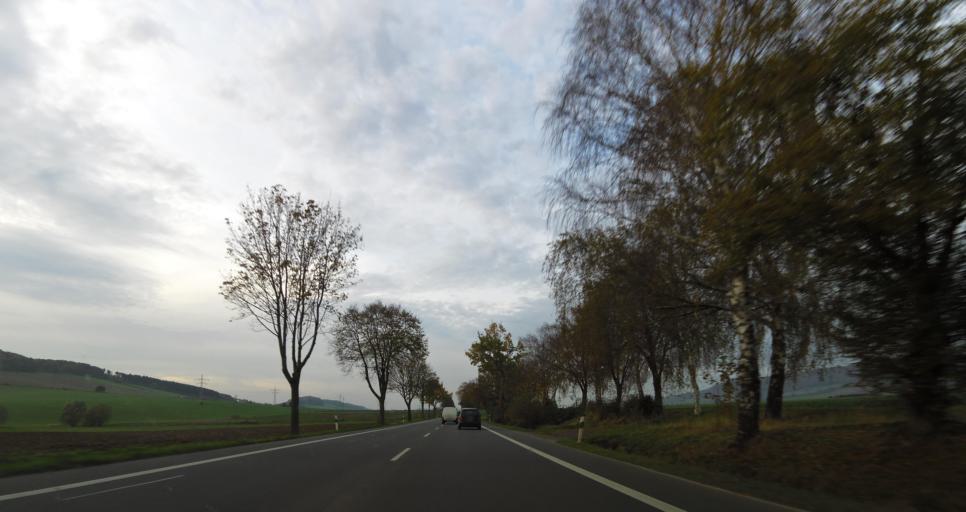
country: DE
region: Lower Saxony
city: Luerdissen
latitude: 51.9553
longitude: 9.6105
